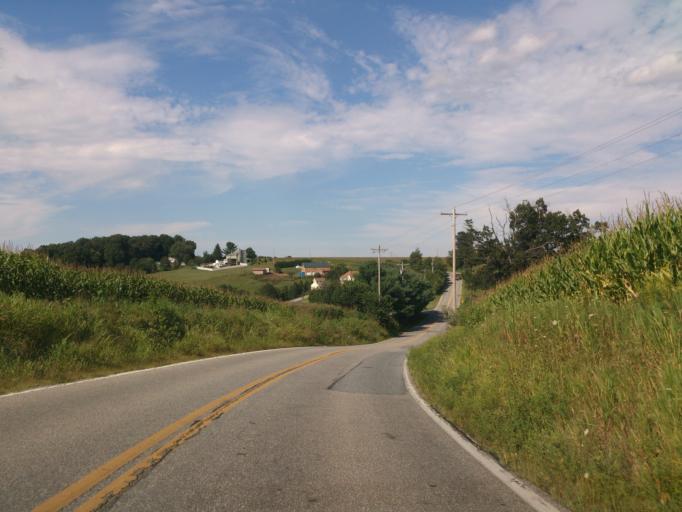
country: US
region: Pennsylvania
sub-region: York County
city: Susquehanna Trails
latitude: 39.7930
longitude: -76.4737
